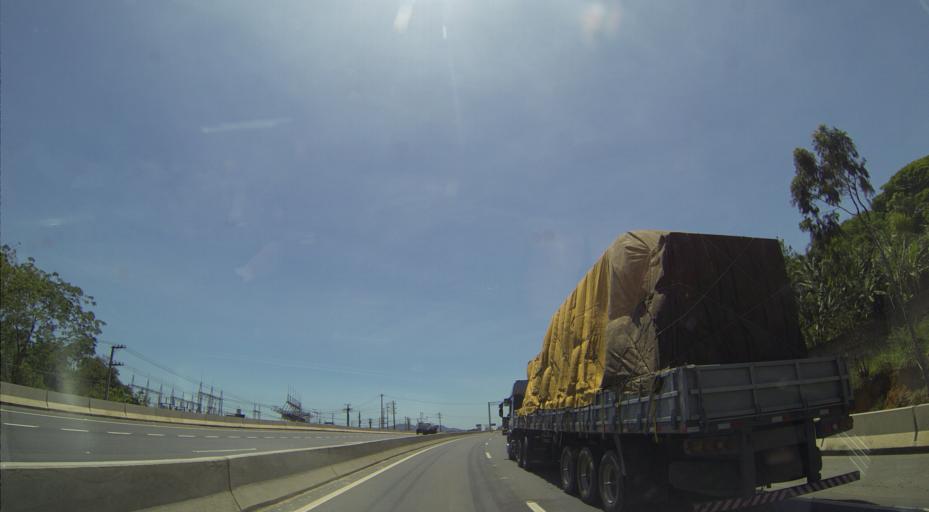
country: BR
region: Espirito Santo
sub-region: Vitoria
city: Vitoria
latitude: -20.3442
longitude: -40.4091
